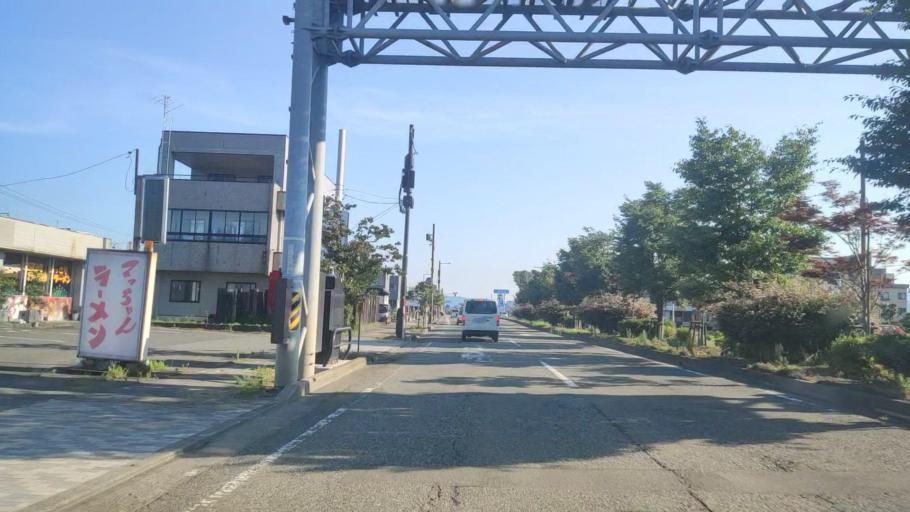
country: JP
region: Fukui
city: Maruoka
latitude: 36.1485
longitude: 136.2648
